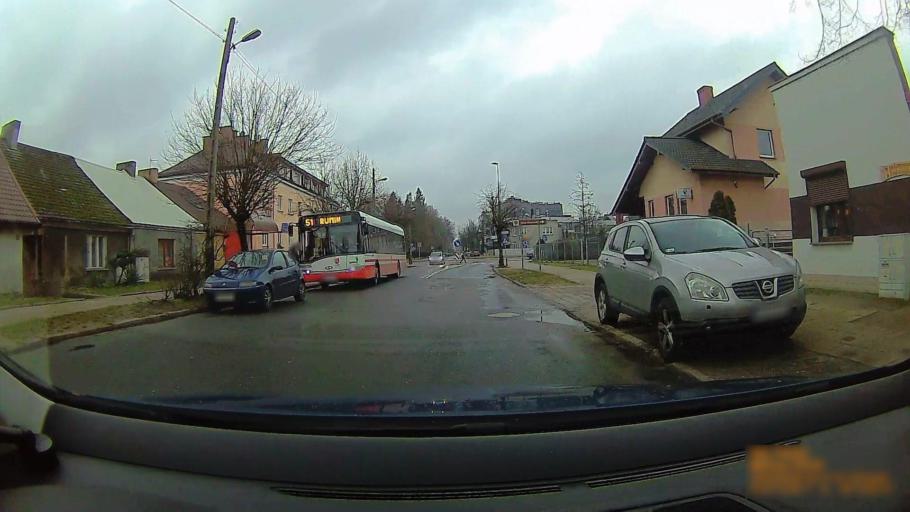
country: PL
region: Greater Poland Voivodeship
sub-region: Konin
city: Konin
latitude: 52.2080
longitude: 18.2464
